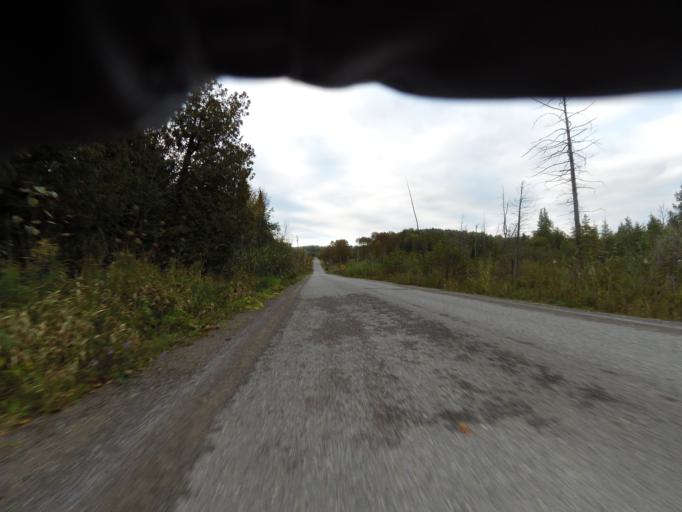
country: CA
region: Ontario
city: Quinte West
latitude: 44.0119
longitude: -77.8100
